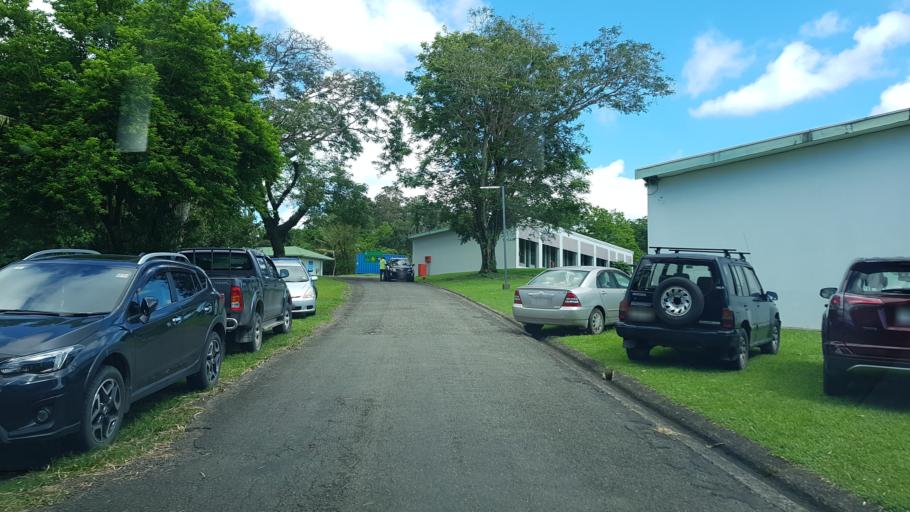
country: FJ
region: Central
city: Suva
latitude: -18.1480
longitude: 178.4428
